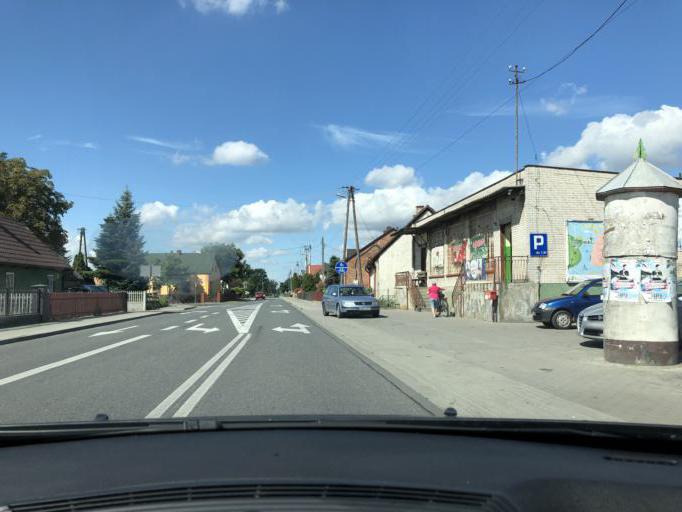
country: PL
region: Lodz Voivodeship
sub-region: Powiat wieruszowski
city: Czastary
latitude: 51.2414
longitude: 18.3257
